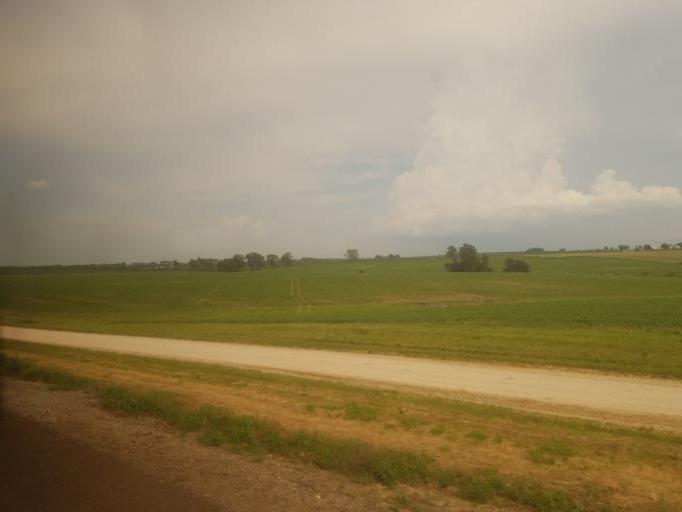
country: US
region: Illinois
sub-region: Henry County
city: Galva
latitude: 41.0887
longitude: -90.2019
